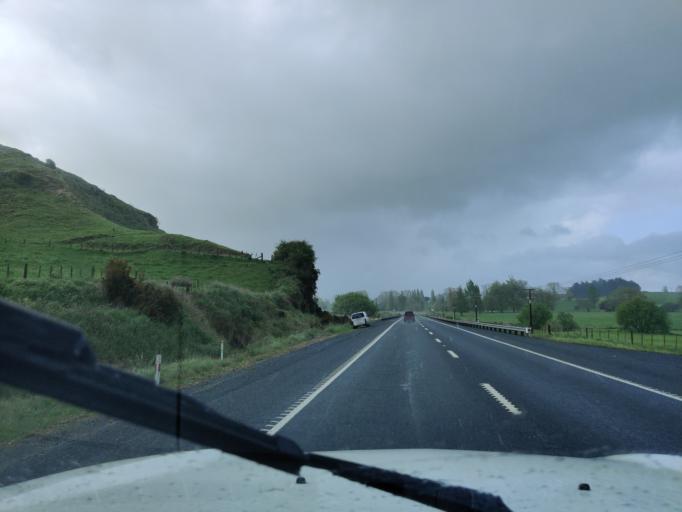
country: NZ
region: Waikato
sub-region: Matamata-Piako District
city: Matamata
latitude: -37.9717
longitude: 175.6927
